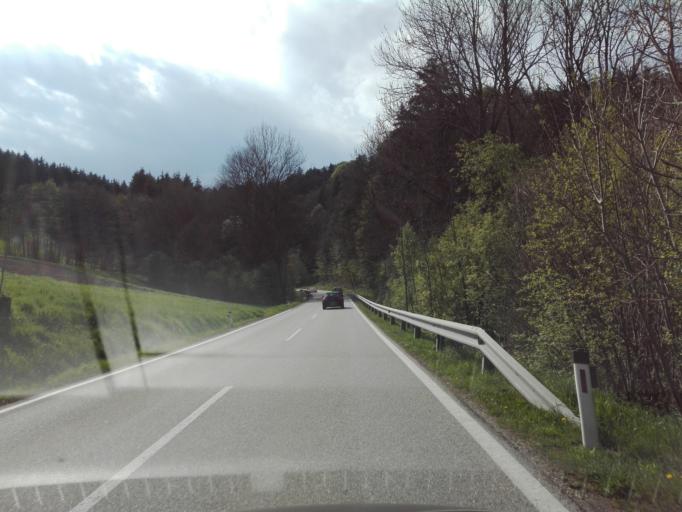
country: AT
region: Upper Austria
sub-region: Politischer Bezirk Urfahr-Umgebung
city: Sankt Gotthard im Muhlkreis
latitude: 48.3844
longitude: 14.0841
